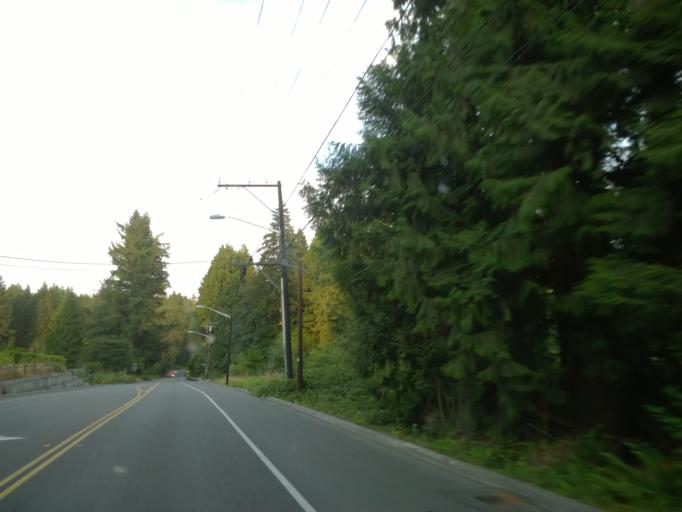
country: US
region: Washington
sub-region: King County
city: Cottage Lake
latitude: 47.7549
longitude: -122.0605
